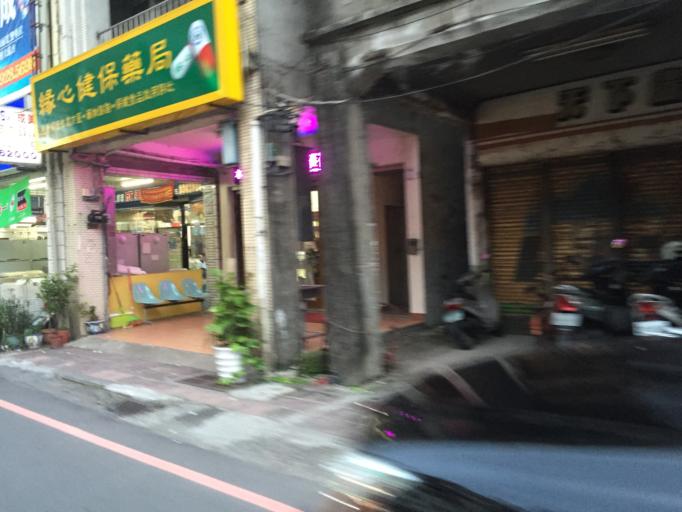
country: TW
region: Taiwan
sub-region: Yilan
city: Yilan
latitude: 24.7628
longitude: 121.7541
